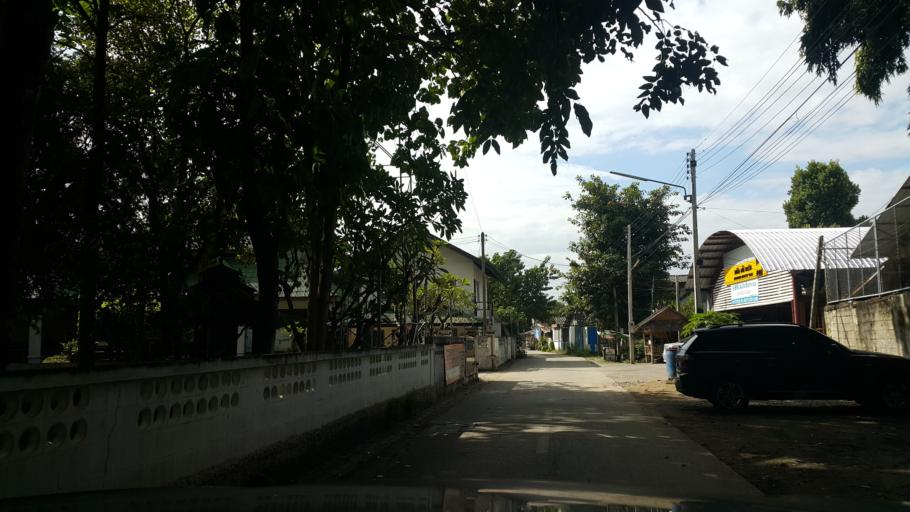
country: TH
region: Chiang Mai
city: Chiang Mai
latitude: 18.7820
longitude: 99.0230
